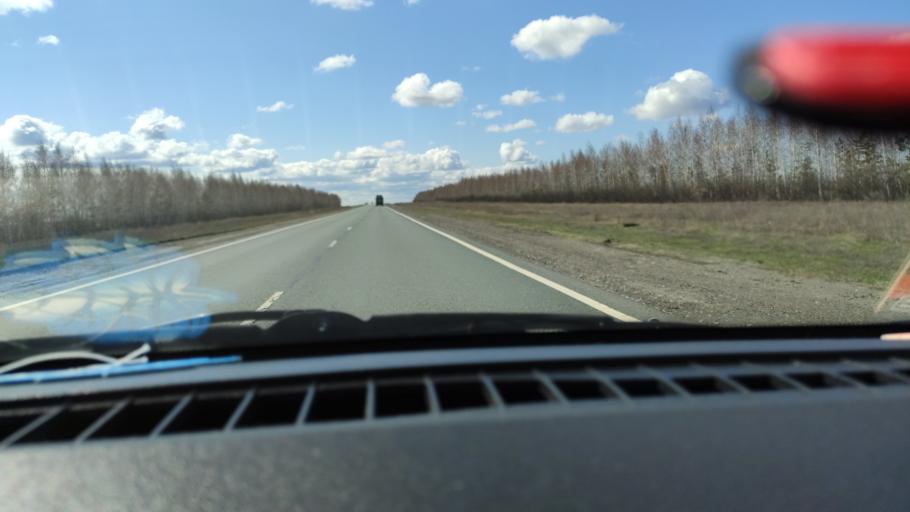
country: RU
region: Saratov
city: Dukhovnitskoye
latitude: 52.8128
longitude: 48.2301
